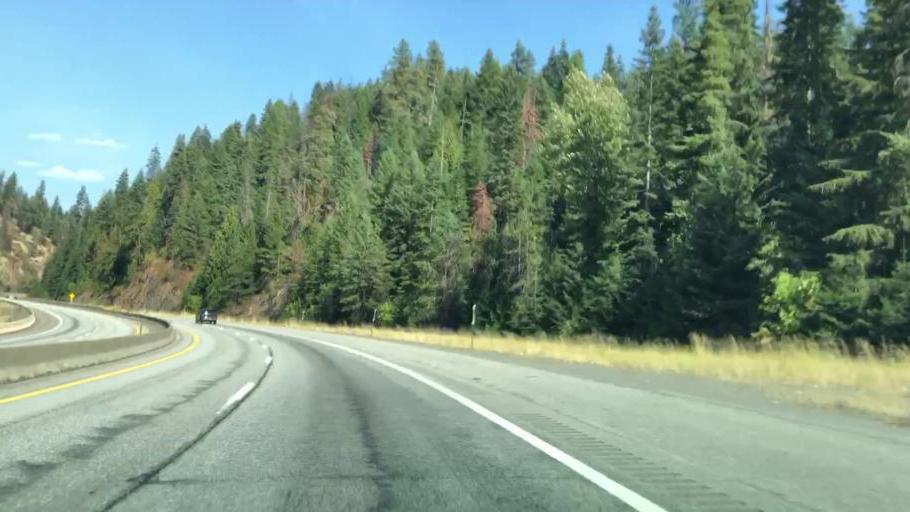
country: US
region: Idaho
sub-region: Kootenai County
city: Coeur d'Alene
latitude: 47.6207
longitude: -116.5767
